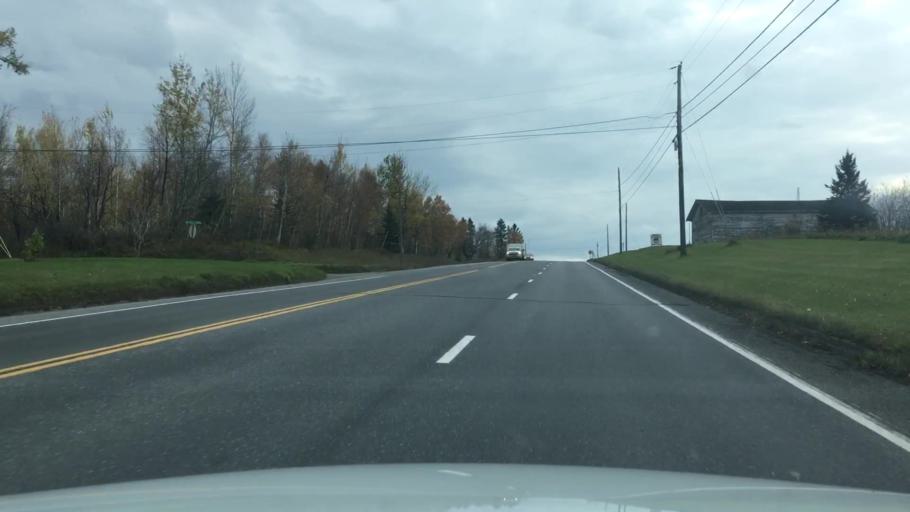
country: US
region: Maine
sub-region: Aroostook County
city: Caribou
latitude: 46.7820
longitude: -67.9890
